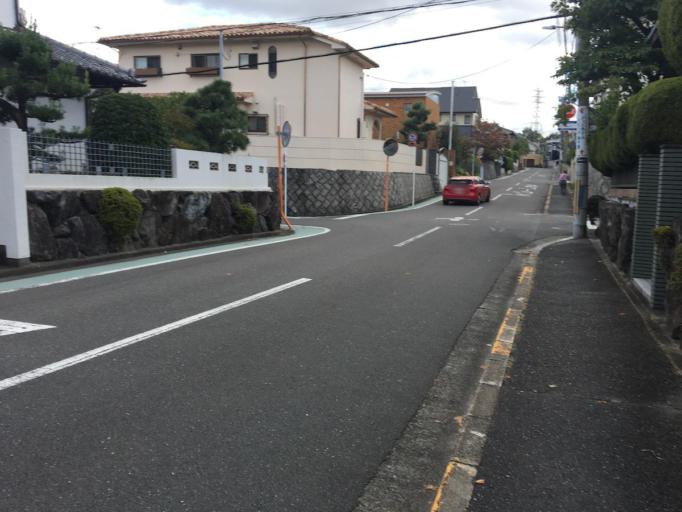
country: JP
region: Osaka
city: Suita
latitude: 34.8013
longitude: 135.5164
